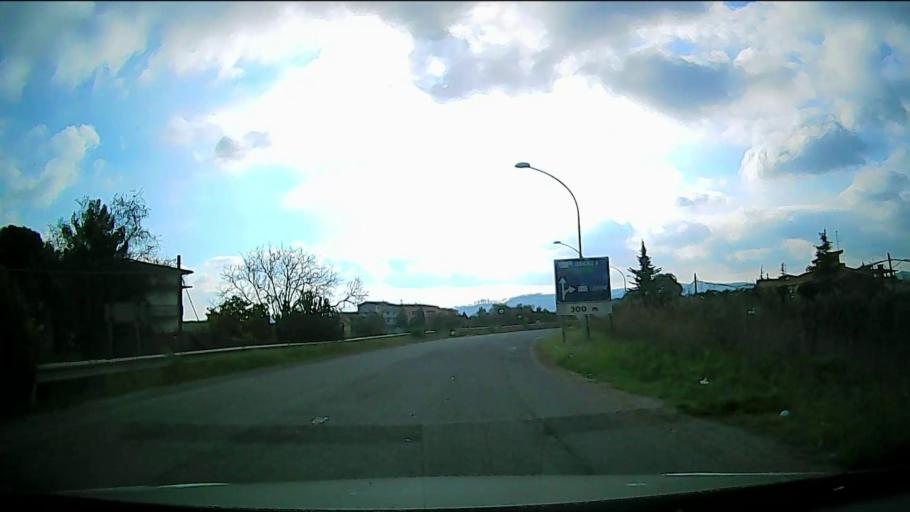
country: IT
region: Calabria
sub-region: Provincia di Crotone
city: Rocca di Neto
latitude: 39.1794
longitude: 17.0172
